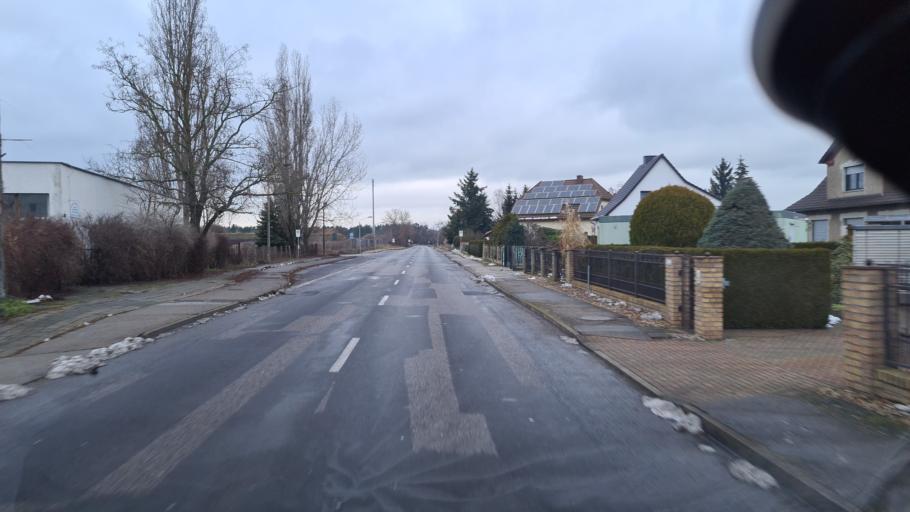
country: DE
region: Brandenburg
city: Eisenhuettenstadt
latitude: 52.1513
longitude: 14.6734
